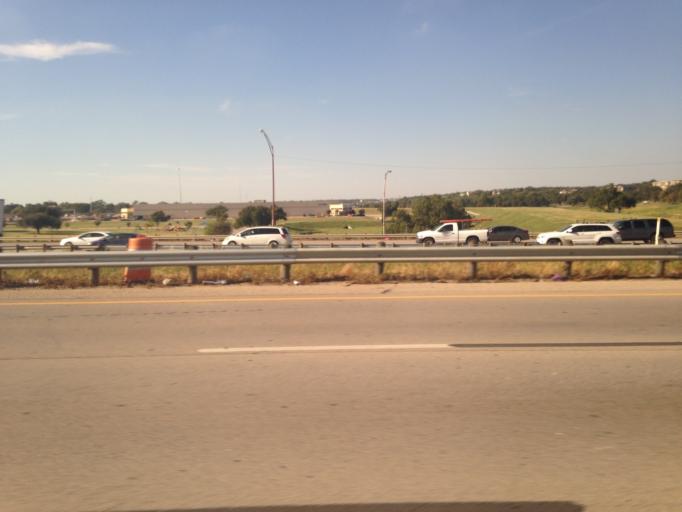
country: US
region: Texas
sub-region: Tarrant County
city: Fort Worth
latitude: 32.7663
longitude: -97.3145
